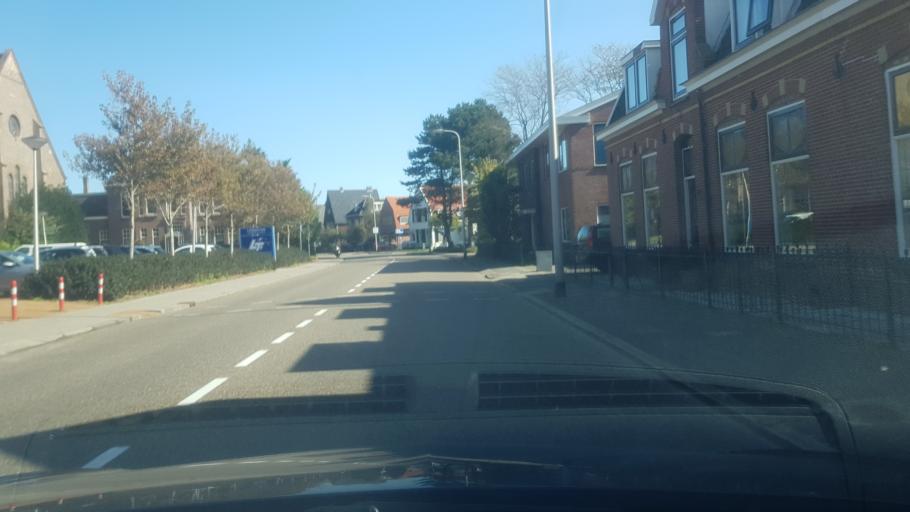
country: NL
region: South Holland
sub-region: Gemeente Noordwijkerhout
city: Noordwijkerhout
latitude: 52.2638
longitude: 4.4947
